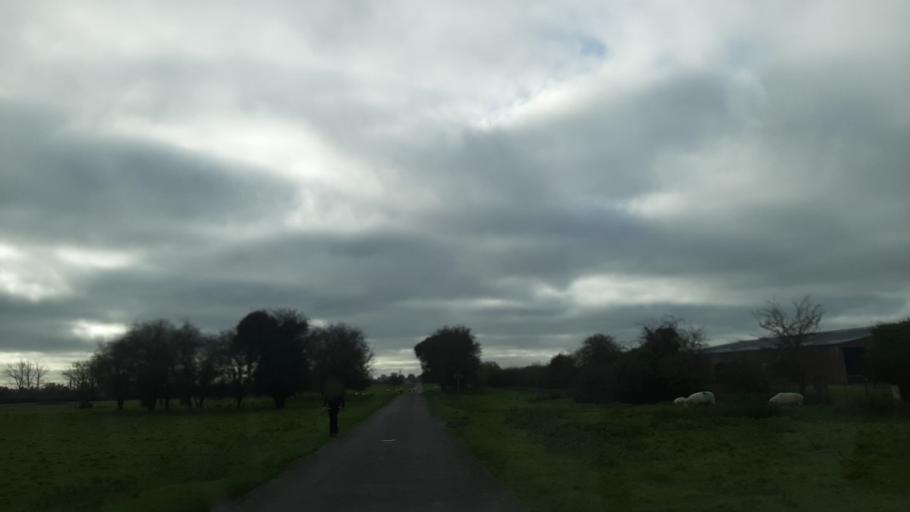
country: IE
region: Leinster
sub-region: Kildare
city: Kildare
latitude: 53.1776
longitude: -6.8964
